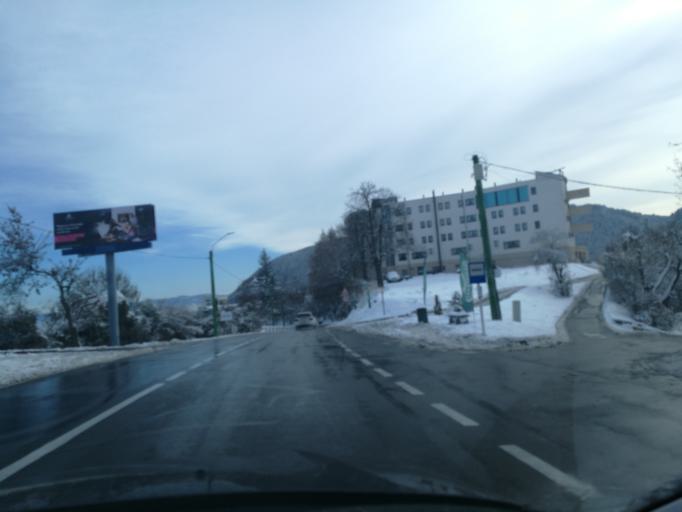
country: RO
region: Brasov
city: Brasov
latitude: 45.6463
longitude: 25.5769
